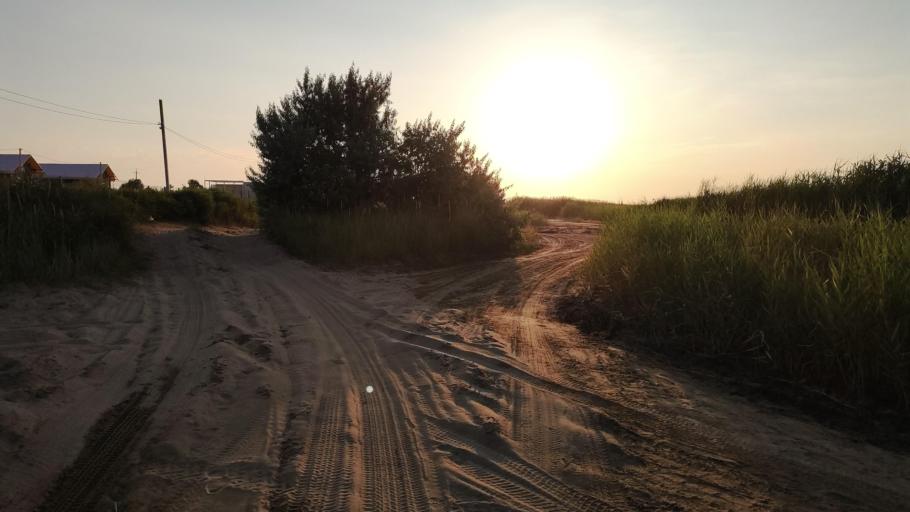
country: RU
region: Krasnodarskiy
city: Blagovetschenskaya
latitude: 45.0674
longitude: 37.0368
